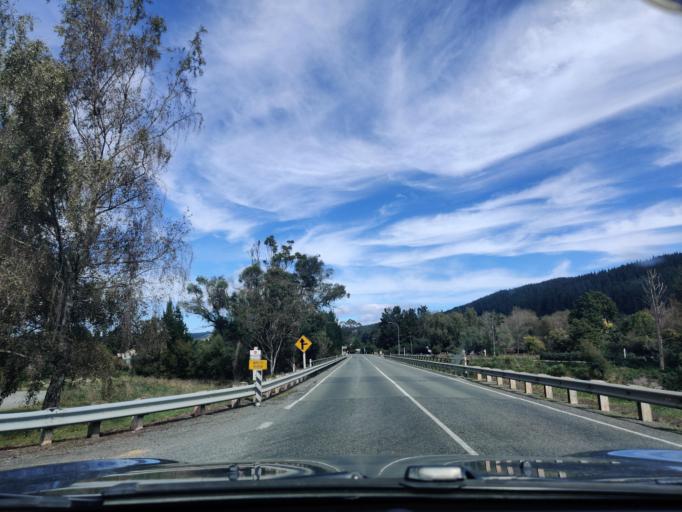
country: NZ
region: Tasman
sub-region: Tasman District
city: Wakefield
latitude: -41.4279
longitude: 172.9918
